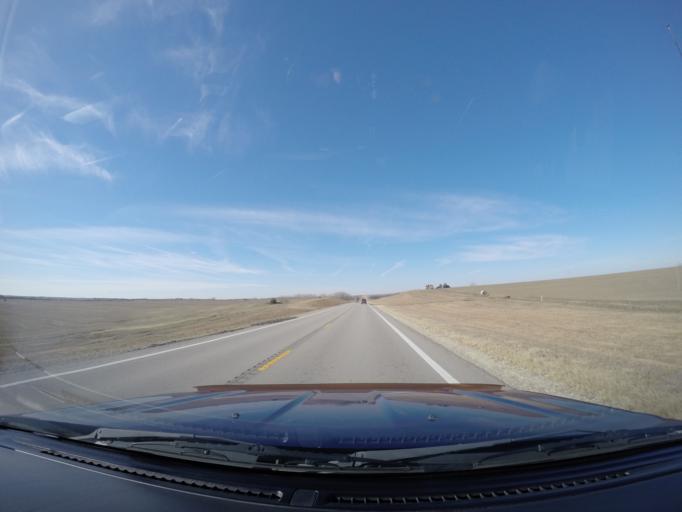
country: US
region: Kansas
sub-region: Clay County
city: Clay Center
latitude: 39.3789
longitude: -97.2976
